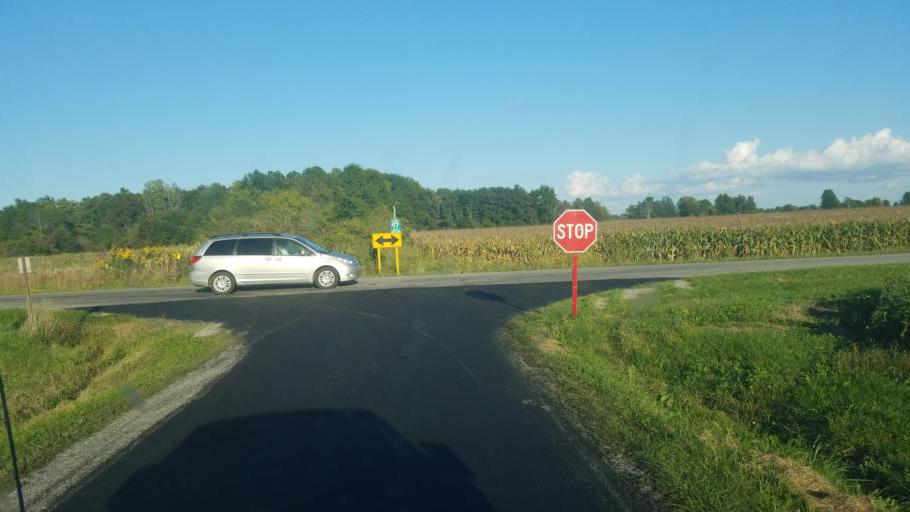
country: US
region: Ohio
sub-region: Wyandot County
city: Carey
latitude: 40.9198
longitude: -83.3820
